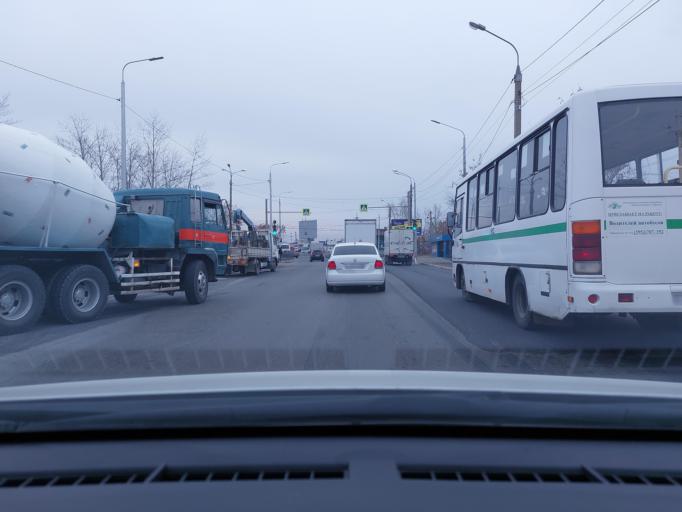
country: RU
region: Irkutsk
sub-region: Irkutskiy Rayon
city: Irkutsk
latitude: 52.3296
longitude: 104.2329
